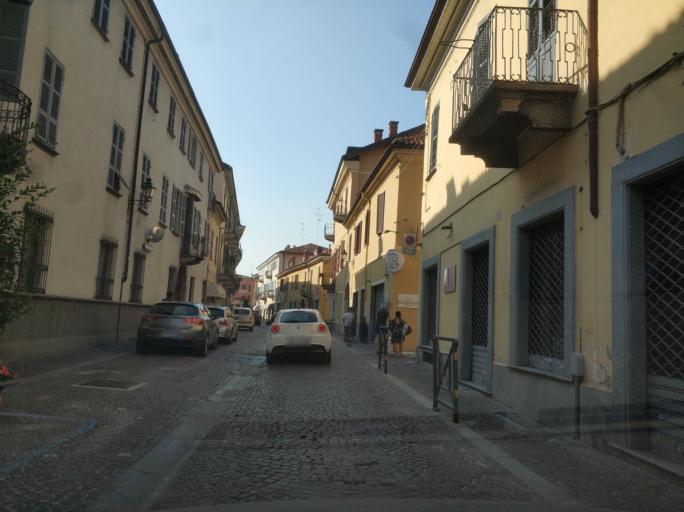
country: IT
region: Piedmont
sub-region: Provincia di Cuneo
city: Bra
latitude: 44.6991
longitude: 7.8500
